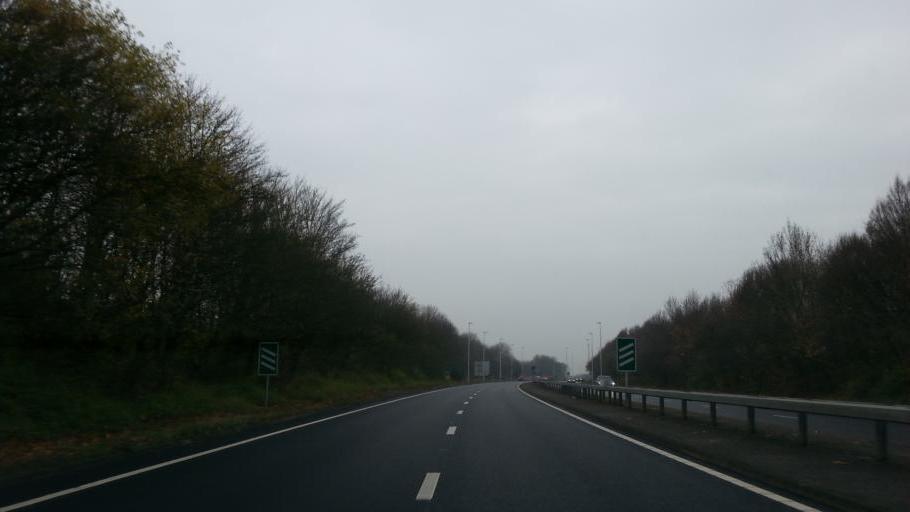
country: GB
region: England
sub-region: Peterborough
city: Castor
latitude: 52.5421
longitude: -0.3053
